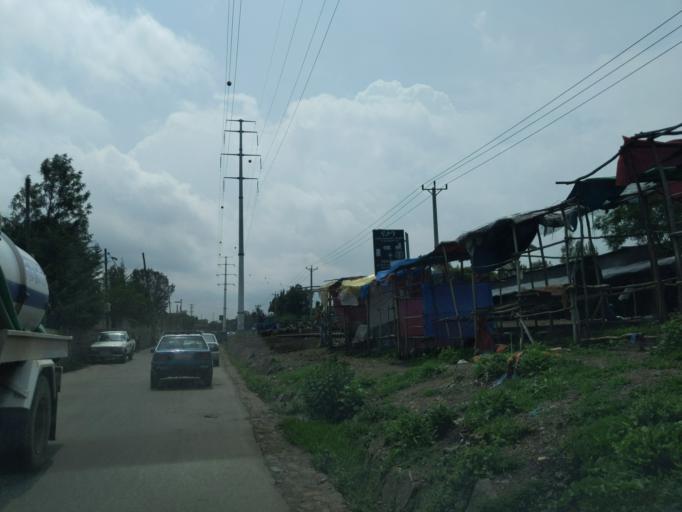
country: ET
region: Adis Abeba
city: Addis Ababa
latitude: 8.9545
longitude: 38.7615
